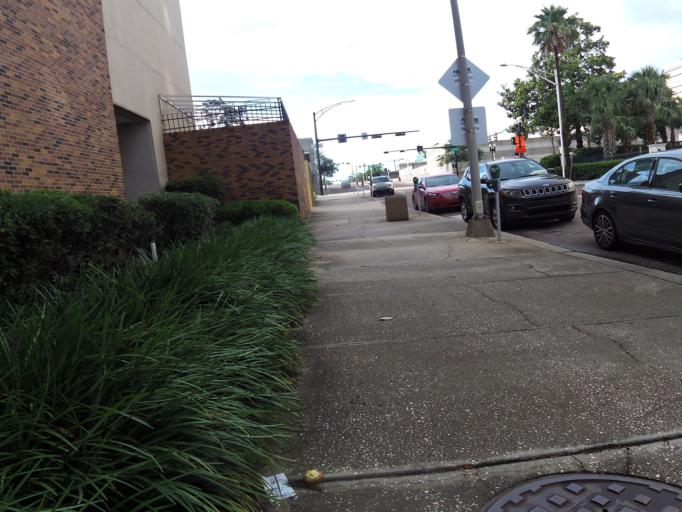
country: US
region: Florida
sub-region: Duval County
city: Jacksonville
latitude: 30.3246
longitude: -81.6531
